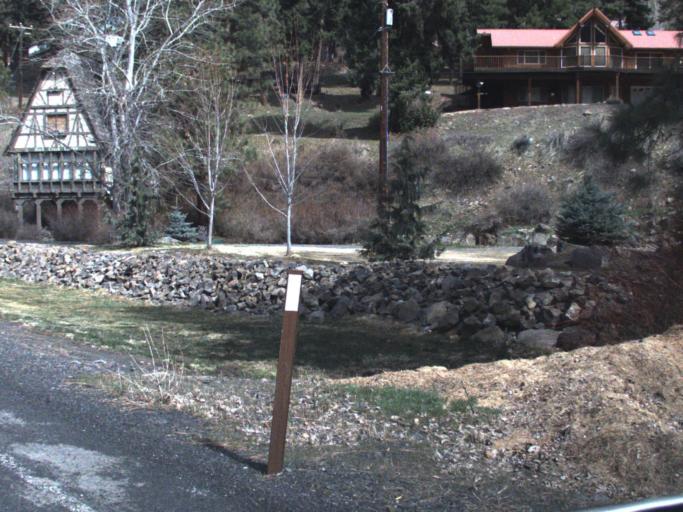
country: US
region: Washington
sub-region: Yakima County
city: Tieton
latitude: 46.8811
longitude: -120.9815
